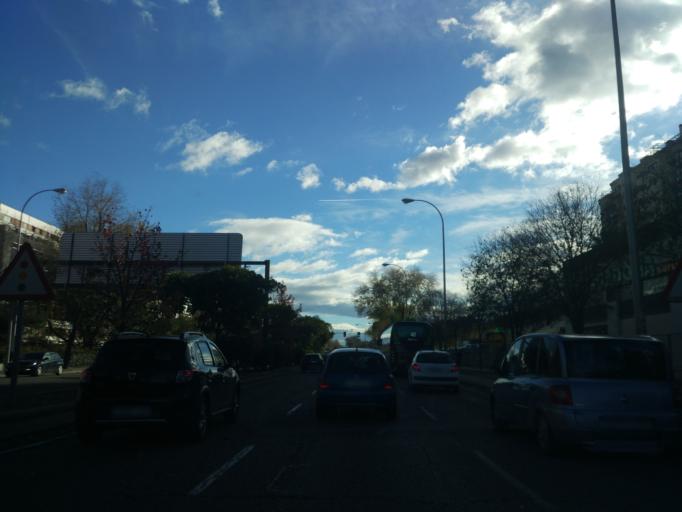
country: ES
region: Madrid
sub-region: Provincia de Madrid
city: Usera
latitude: 40.3724
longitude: -3.6948
